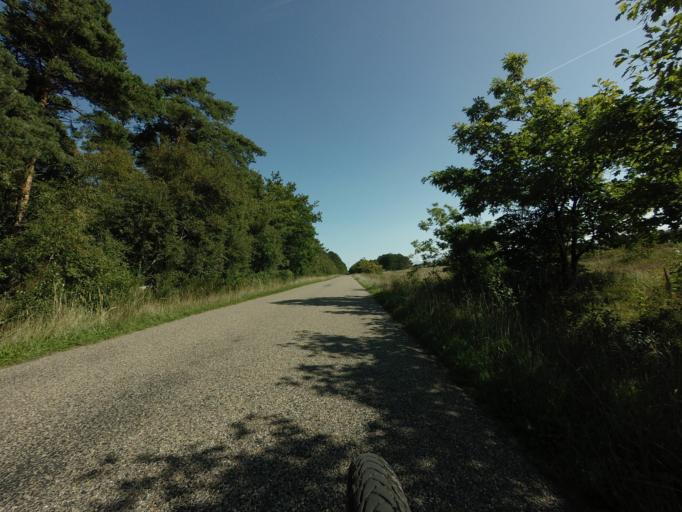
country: DK
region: North Denmark
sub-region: Hjorring Kommune
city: Hirtshals
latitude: 57.5792
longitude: 10.0140
